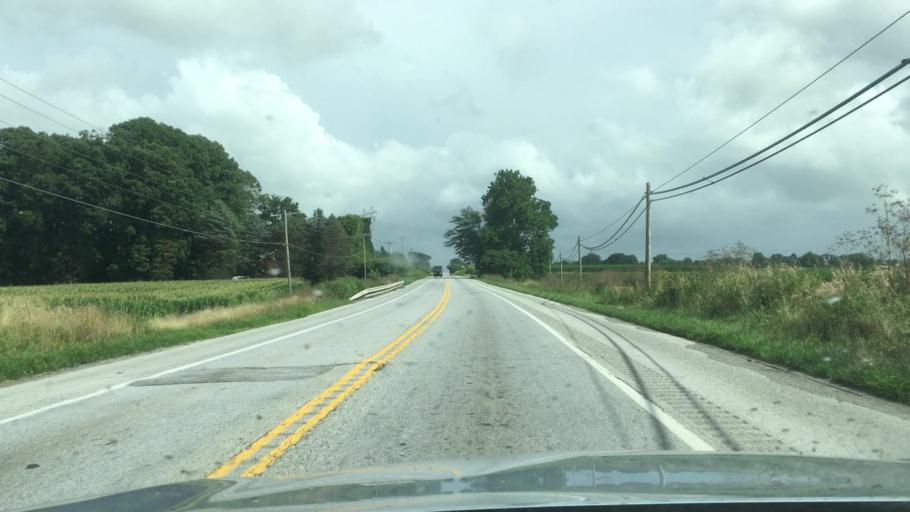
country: US
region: Pennsylvania
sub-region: Chester County
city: Parkesburg
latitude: 39.9034
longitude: -75.9304
